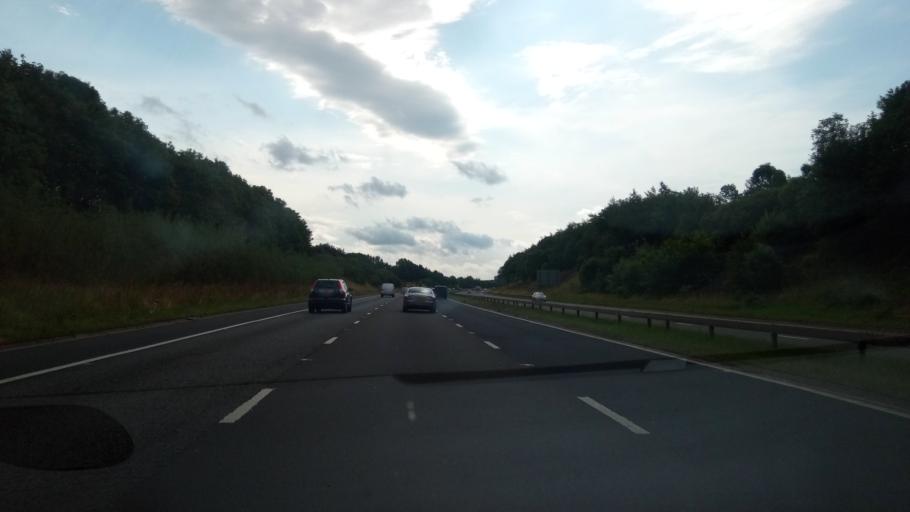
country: GB
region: England
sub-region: Cumbria
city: Penrith
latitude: 54.6468
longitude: -2.7448
